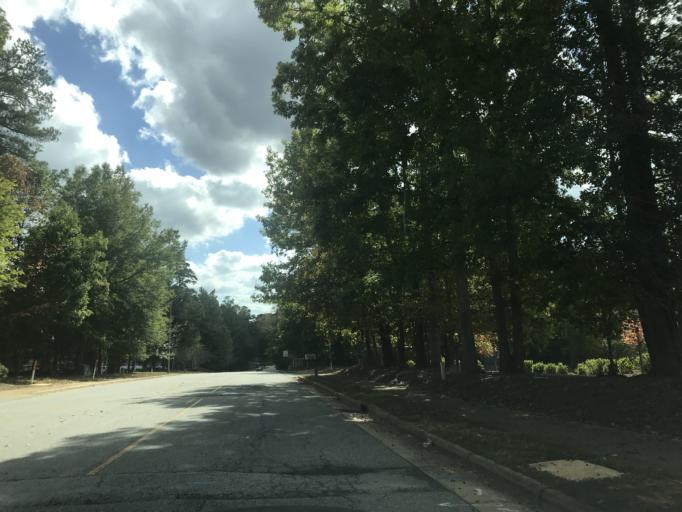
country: US
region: North Carolina
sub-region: Wake County
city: Raleigh
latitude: 35.7298
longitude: -78.6578
